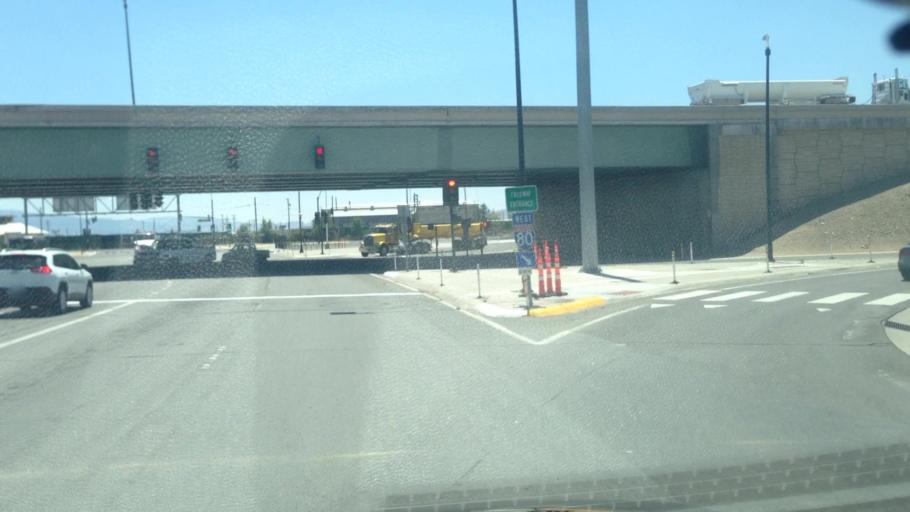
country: US
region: Nevada
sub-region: Washoe County
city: Sparks
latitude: 39.5346
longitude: -119.7531
